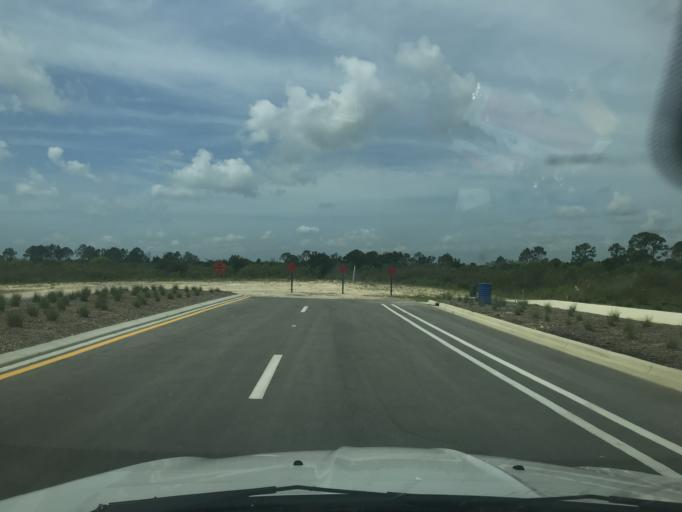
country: US
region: Florida
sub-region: Lee County
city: Olga
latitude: 26.7762
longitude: -81.7432
